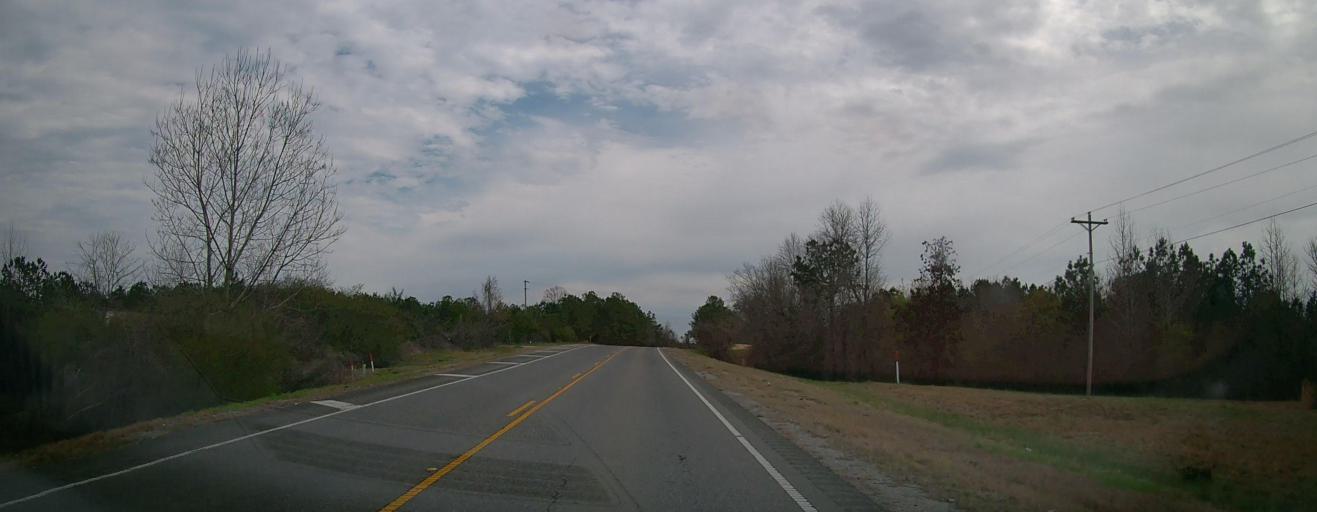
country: US
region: Alabama
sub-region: Marion County
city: Guin
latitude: 34.0300
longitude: -87.9432
